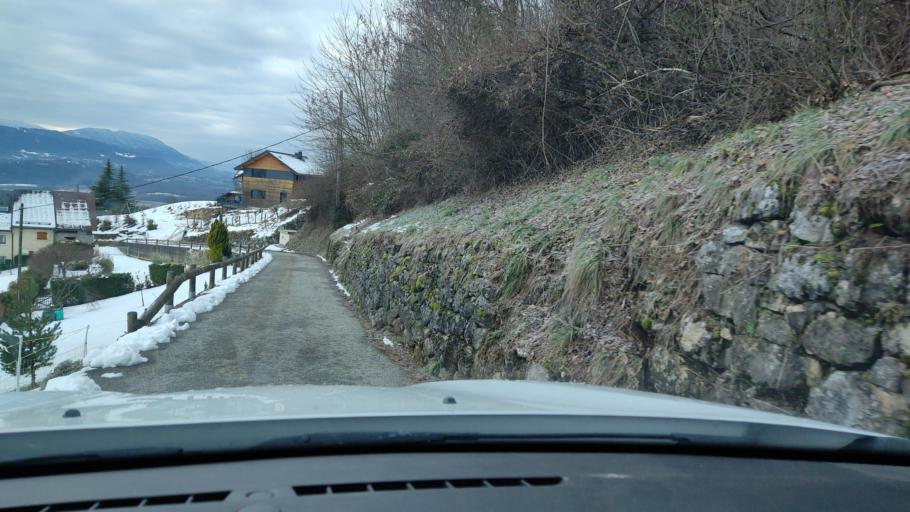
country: FR
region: Rhone-Alpes
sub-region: Departement de la Savoie
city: Coise-Saint-Jean-Pied-Gauthier
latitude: 45.5700
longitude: 6.1362
